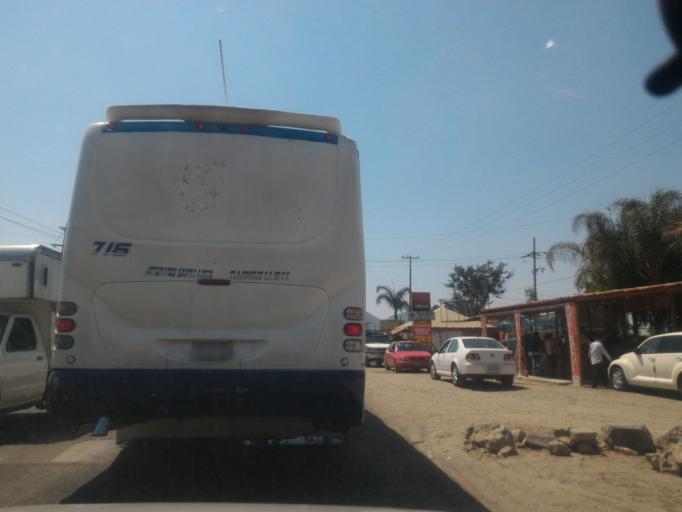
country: MX
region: Jalisco
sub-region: San Pedro Tlaquepaque
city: Santa Anita
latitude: 20.5590
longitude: -103.4169
